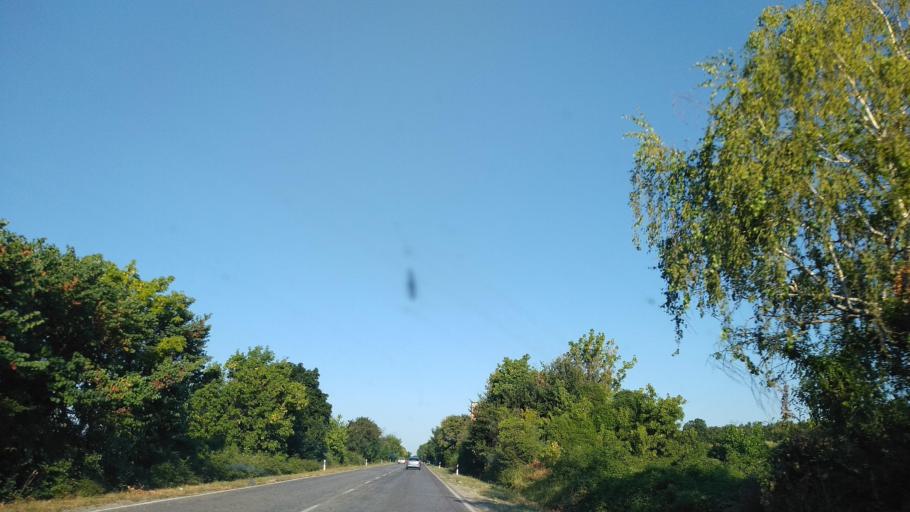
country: BG
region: Gabrovo
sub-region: Obshtina Dryanovo
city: Dryanovo
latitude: 43.0874
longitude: 25.4502
